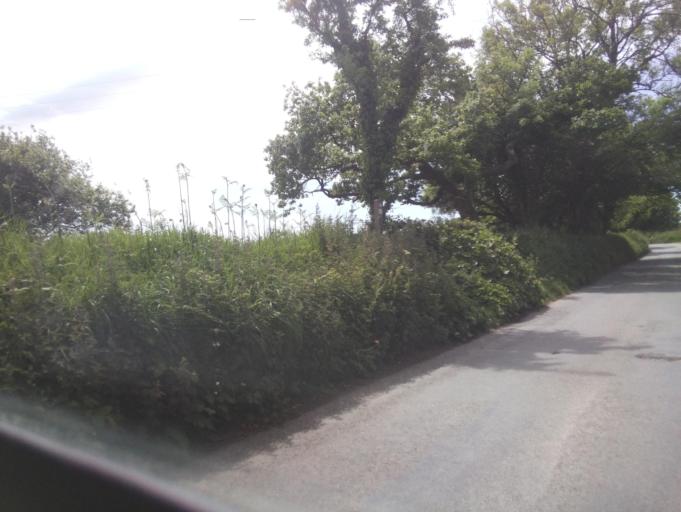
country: GB
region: England
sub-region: Devon
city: Kingsbridge
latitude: 50.3615
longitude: -3.7399
